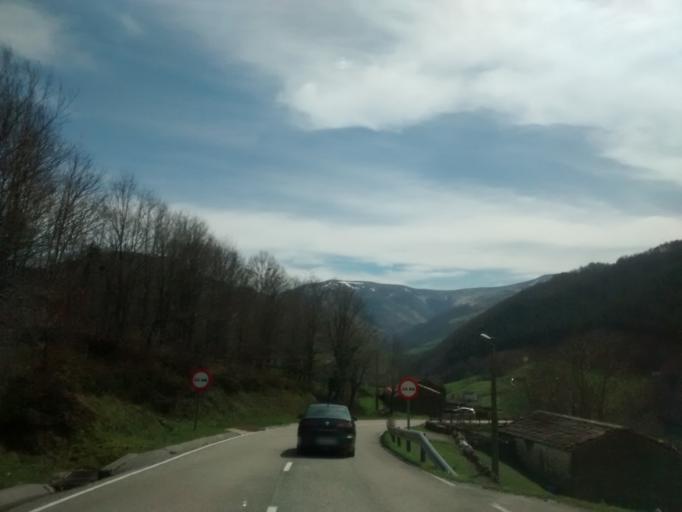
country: ES
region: Cantabria
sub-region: Provincia de Cantabria
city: Vega de Pas
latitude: 43.1628
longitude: -3.7925
